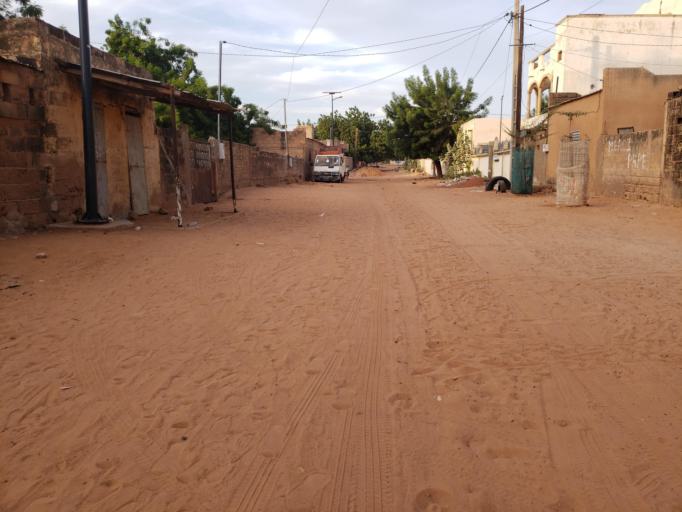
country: SN
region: Louga
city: Ndibene Dahra
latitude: 15.3957
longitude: -15.1126
